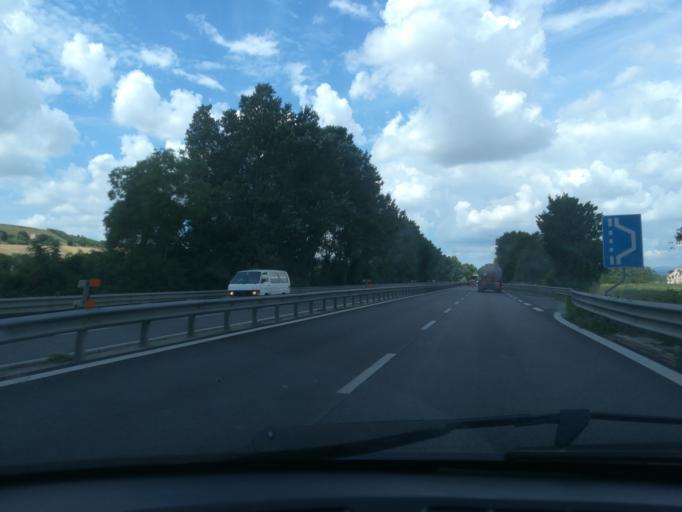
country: IT
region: The Marches
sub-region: Provincia di Macerata
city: Villa San Filippo
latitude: 43.2630
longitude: 13.5724
